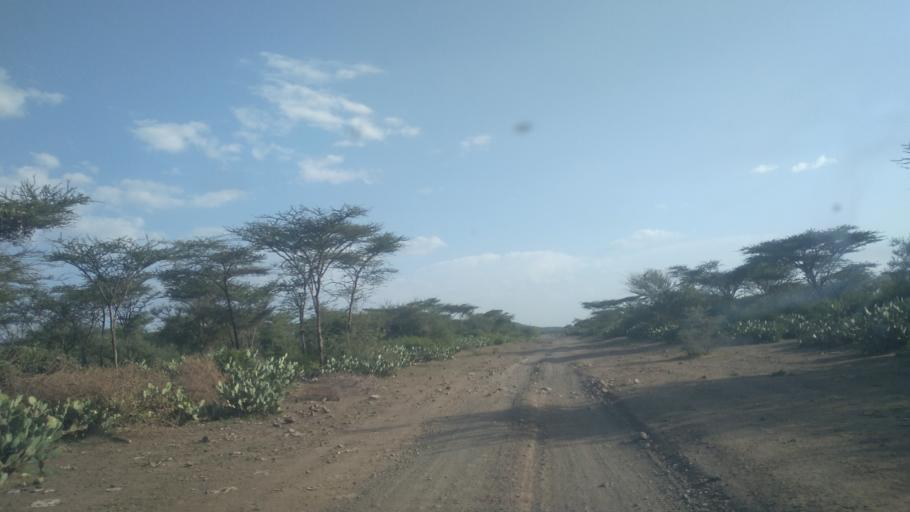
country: ET
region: Oromiya
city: Hirna
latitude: 9.4149
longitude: 40.9585
